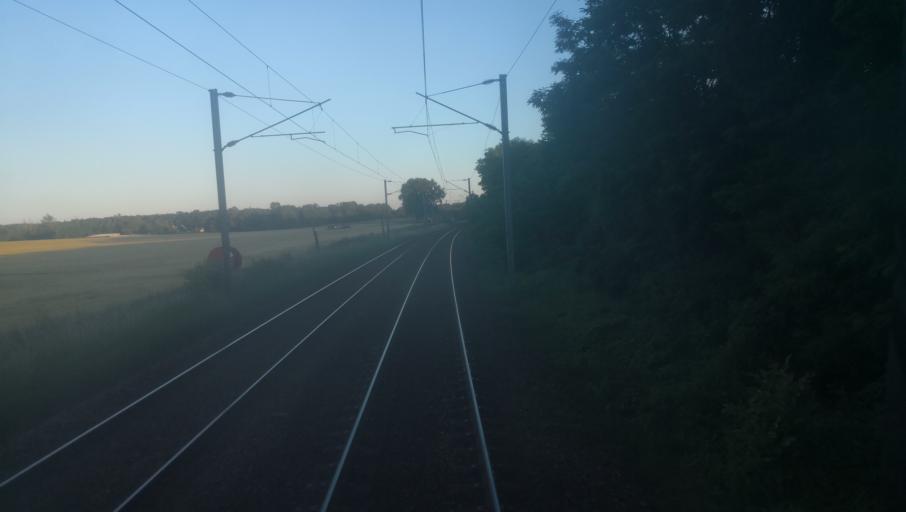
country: FR
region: Bourgogne
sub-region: Departement de la Nievre
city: La Charite-sur-Loire
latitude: 47.2250
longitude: 3.0161
